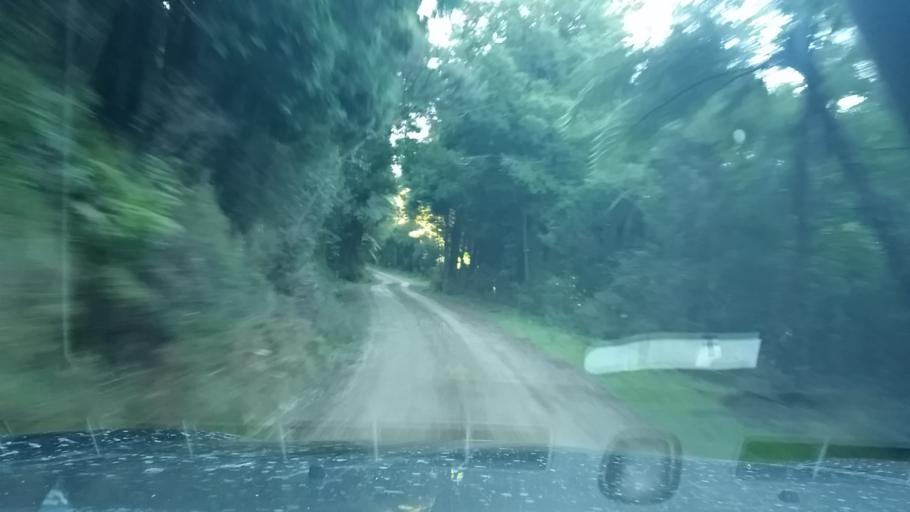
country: NZ
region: Marlborough
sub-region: Marlborough District
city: Picton
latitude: -41.0561
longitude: 174.1092
